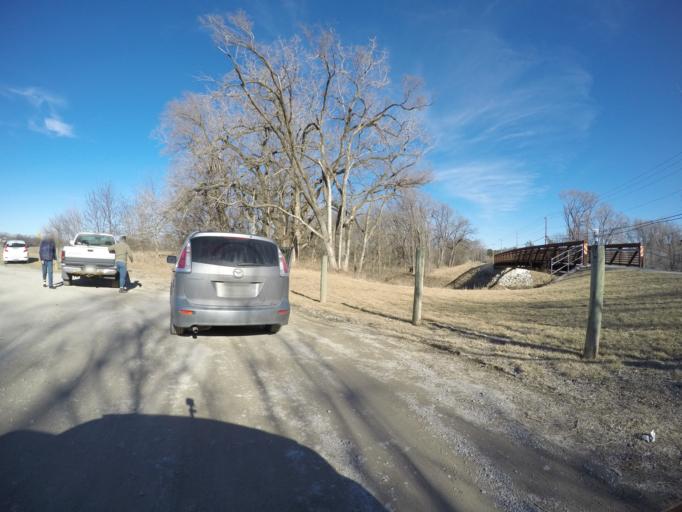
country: US
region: Nebraska
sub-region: Lancaster County
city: Lincoln
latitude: 40.7846
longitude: -96.7370
